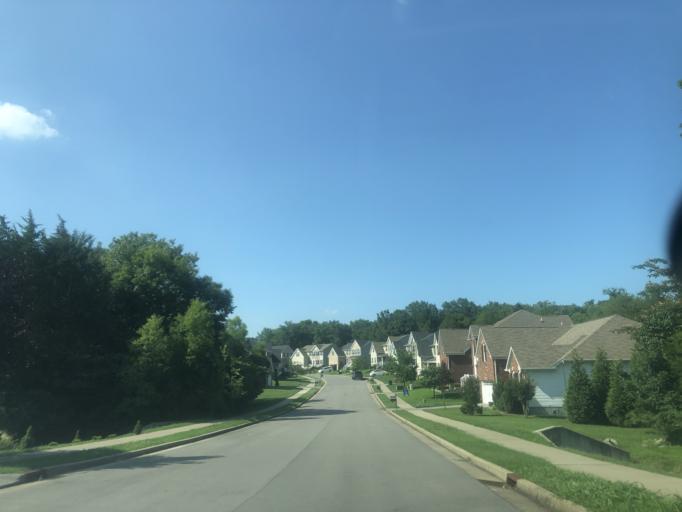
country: US
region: Tennessee
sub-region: Wilson County
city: Green Hill
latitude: 36.1472
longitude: -86.5887
